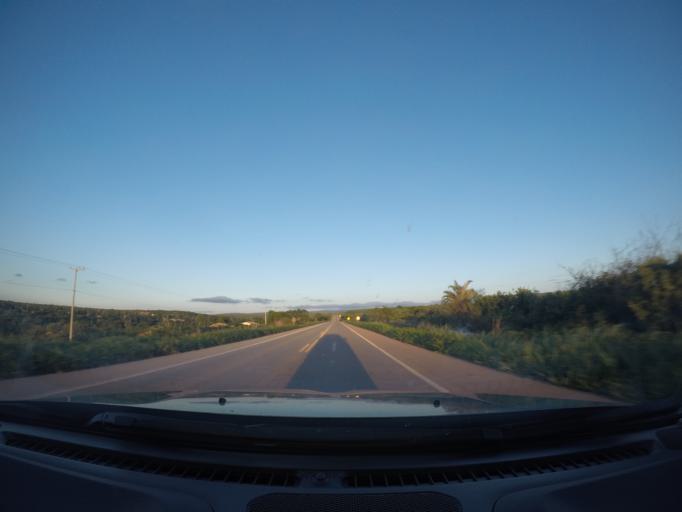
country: BR
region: Bahia
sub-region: Seabra
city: Seabra
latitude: -12.3973
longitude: -41.9358
